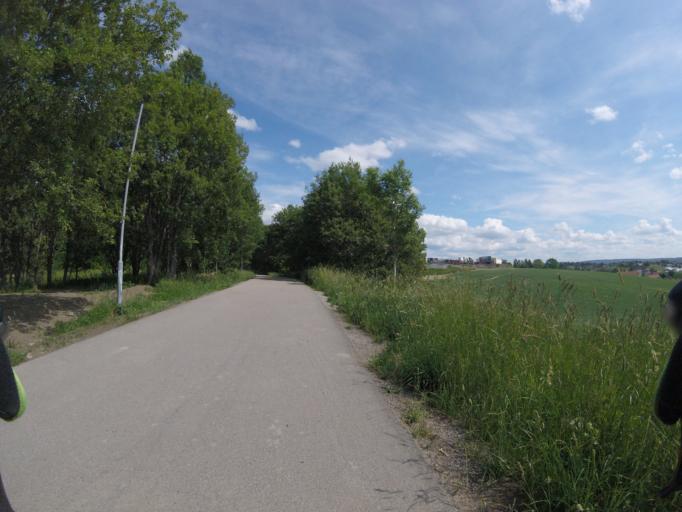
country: NO
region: Akershus
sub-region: Skedsmo
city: Lillestrom
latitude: 59.9832
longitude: 11.0339
